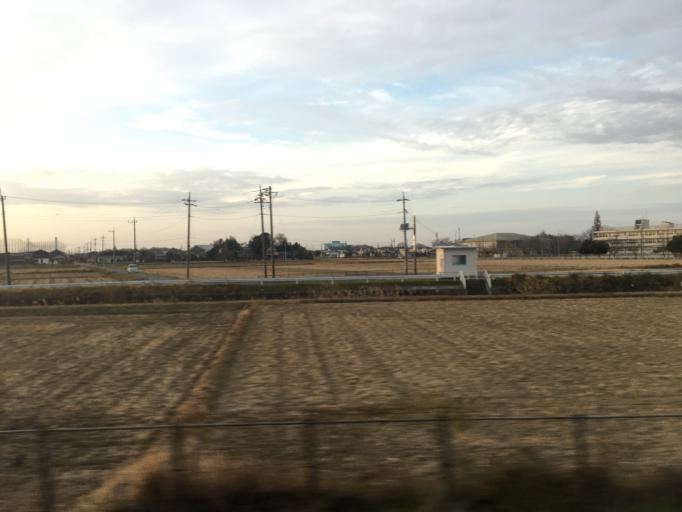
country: JP
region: Saitama
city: Kurihashi
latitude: 36.1163
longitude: 139.6838
